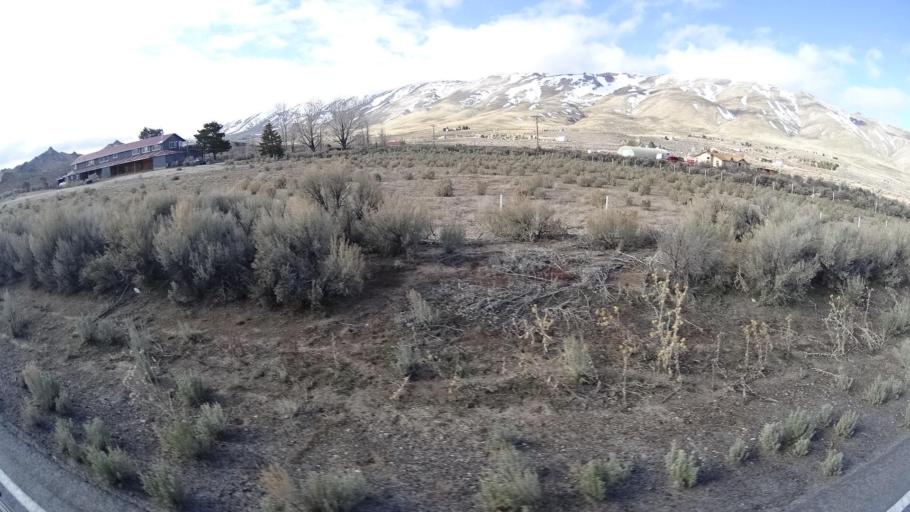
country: US
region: Nevada
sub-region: Washoe County
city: Cold Springs
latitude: 39.8691
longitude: -119.9525
